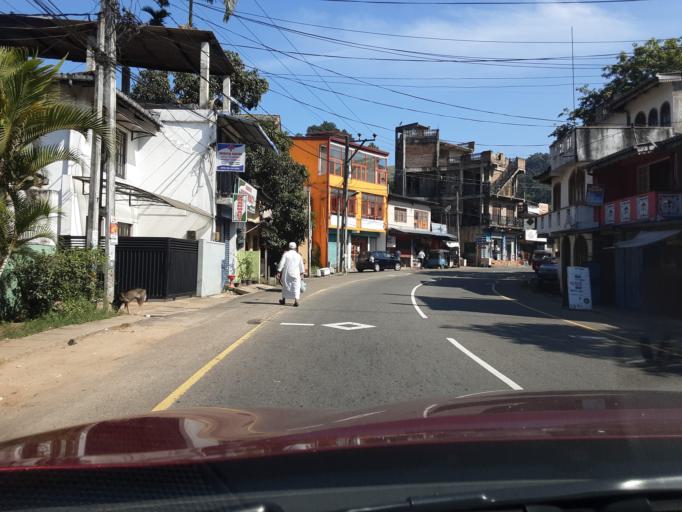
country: LK
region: Uva
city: Badulla
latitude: 7.0012
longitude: 81.0566
